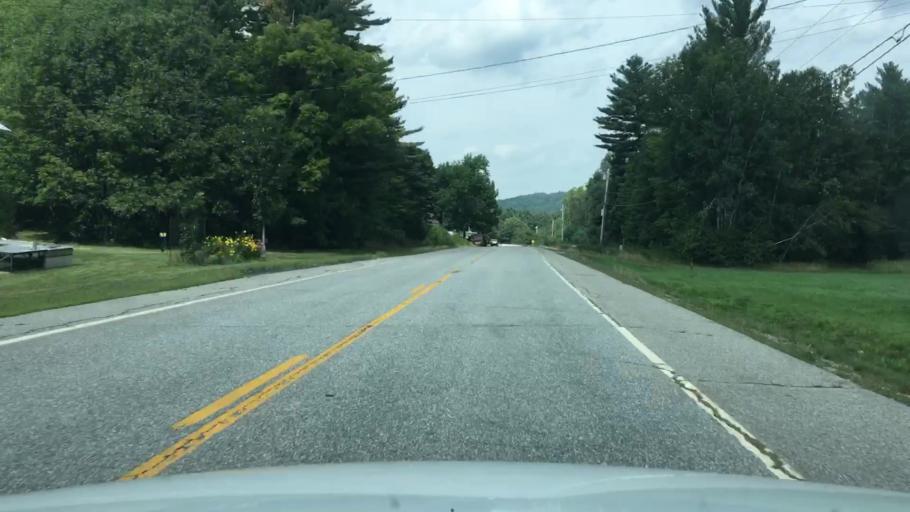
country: US
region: Maine
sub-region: Oxford County
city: Rumford
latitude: 44.5625
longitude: -70.7159
